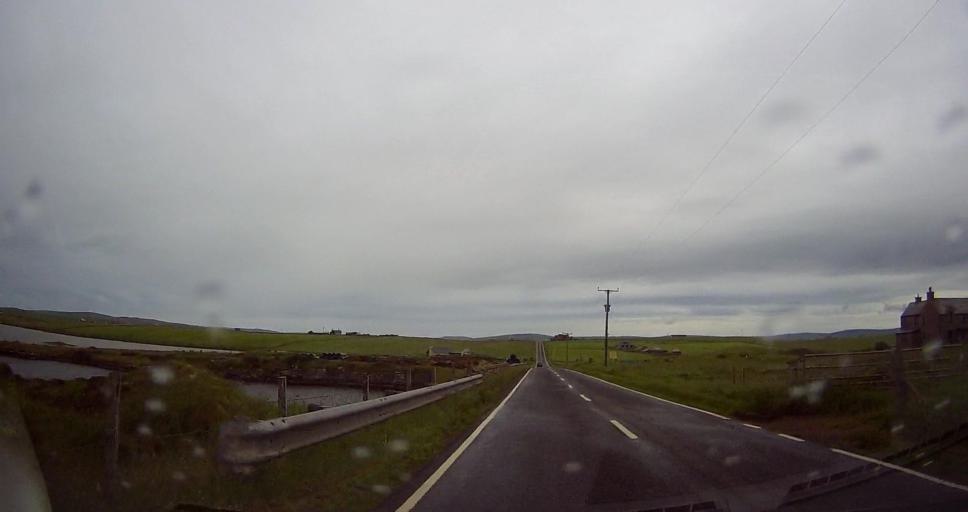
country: GB
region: Scotland
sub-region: Orkney Islands
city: Stromness
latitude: 59.0243
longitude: -3.2955
